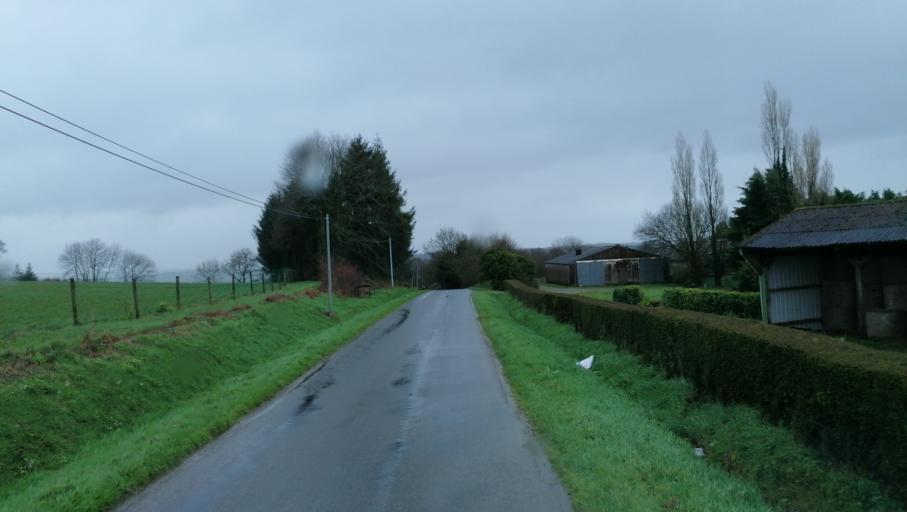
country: FR
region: Brittany
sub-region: Departement des Cotes-d'Armor
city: Plouagat
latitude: 48.4858
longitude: -2.9732
